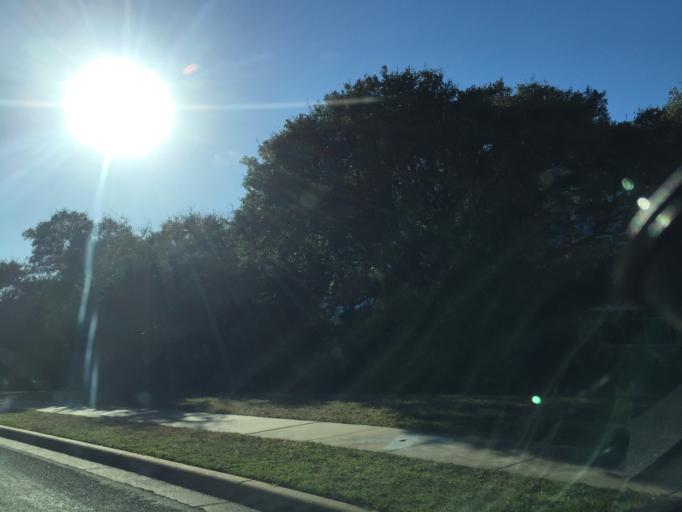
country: US
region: Texas
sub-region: Williamson County
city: Jollyville
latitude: 30.4284
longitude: -97.7524
